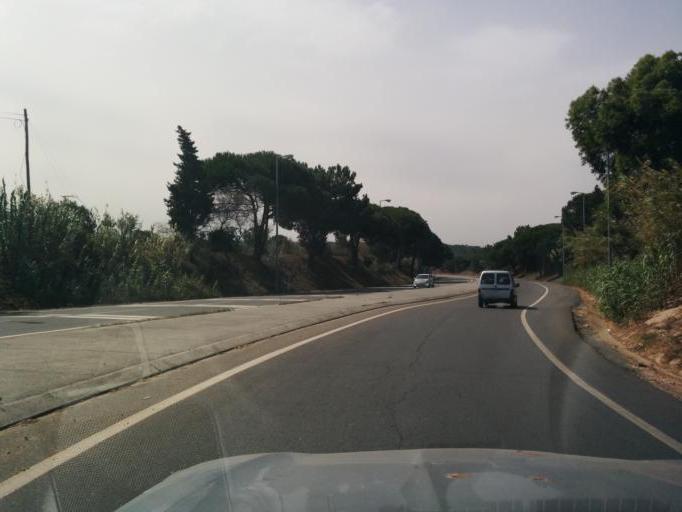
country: PT
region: Beja
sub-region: Odemira
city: Vila Nova de Milfontes
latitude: 37.7329
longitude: -8.7717
